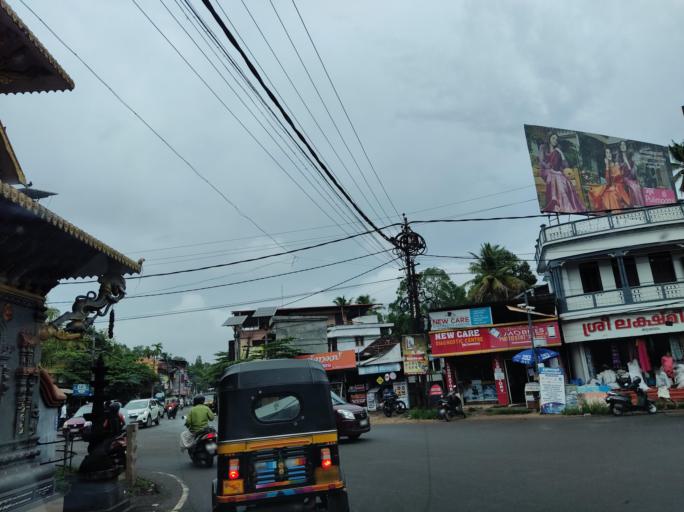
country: IN
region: Kerala
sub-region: Alappuzha
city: Mavelikara
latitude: 9.2512
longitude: 76.5215
